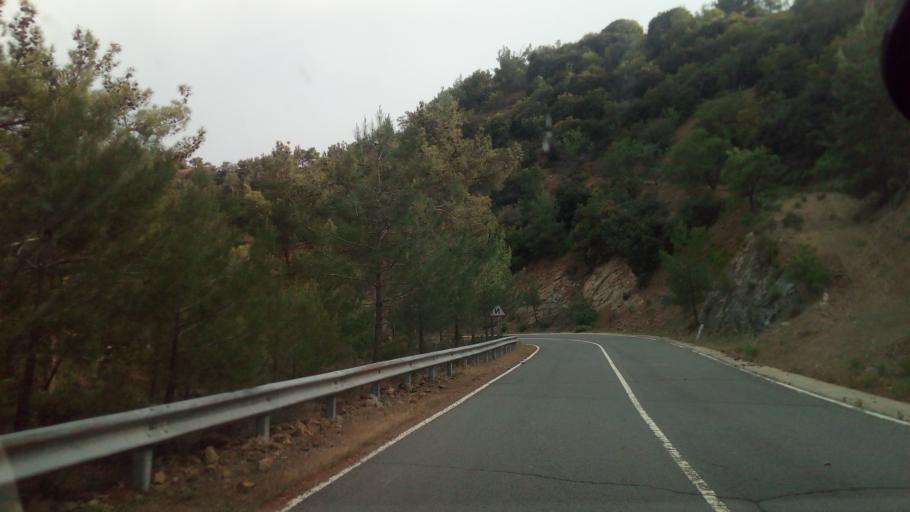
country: CY
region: Lefkosia
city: Kakopetria
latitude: 35.0028
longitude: 32.7915
